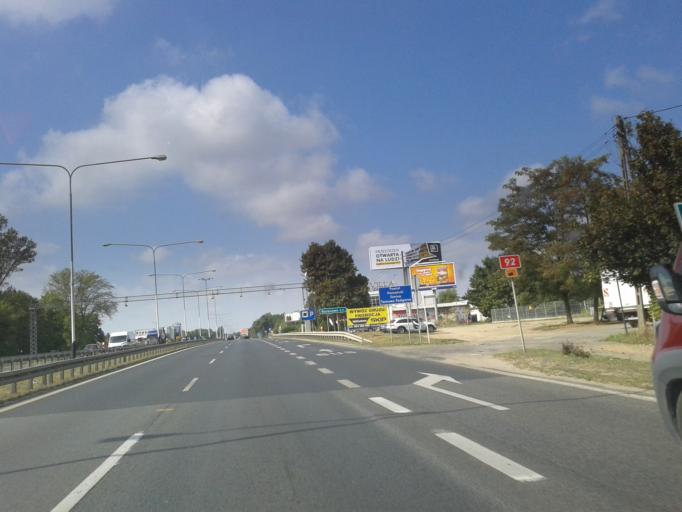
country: PL
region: Greater Poland Voivodeship
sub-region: Powiat poznanski
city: Baranowo
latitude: 52.4335
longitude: 16.7997
